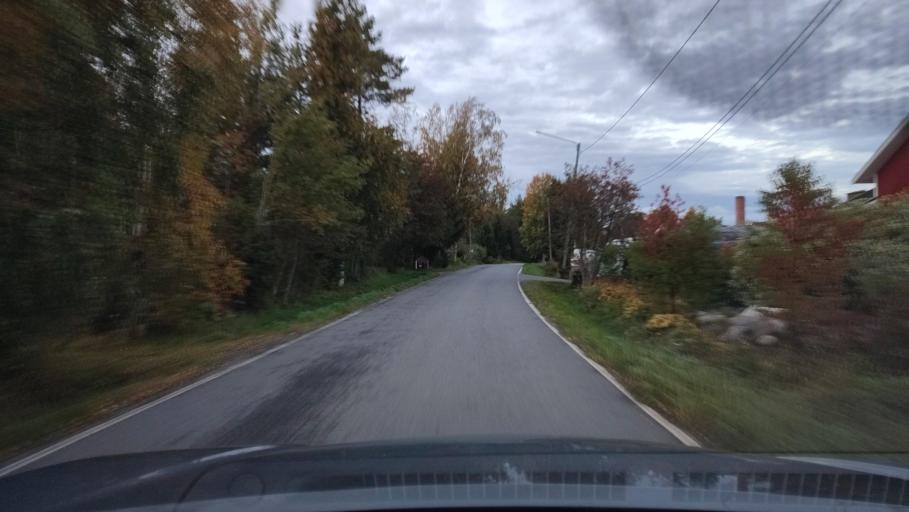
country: FI
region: Ostrobothnia
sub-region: Sydosterbotten
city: Kristinestad
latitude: 62.2716
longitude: 21.5102
